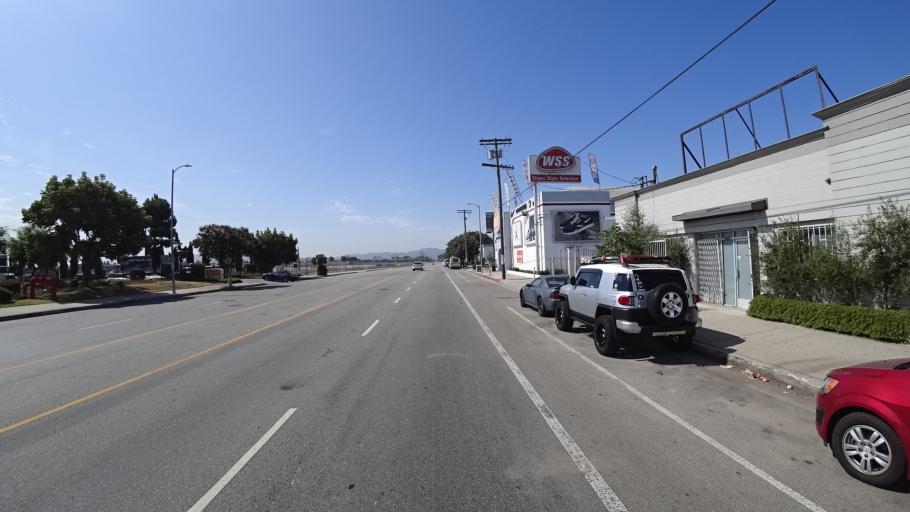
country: US
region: California
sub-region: Los Angeles County
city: North Hollywood
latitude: 34.2002
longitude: -118.3704
